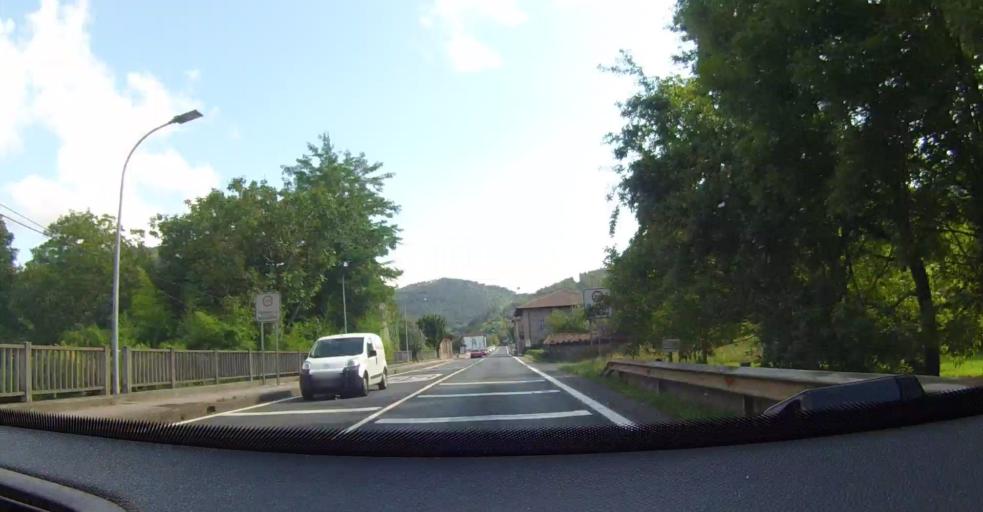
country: ES
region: Basque Country
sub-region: Bizkaia
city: Muxika
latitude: 43.2723
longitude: -2.6853
